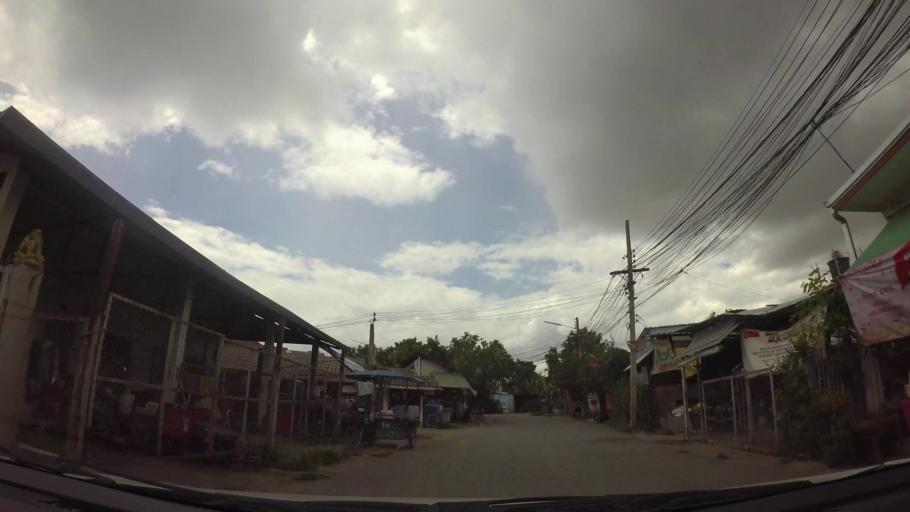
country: TH
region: Chiang Mai
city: Saraphi
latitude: 18.7520
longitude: 99.0391
